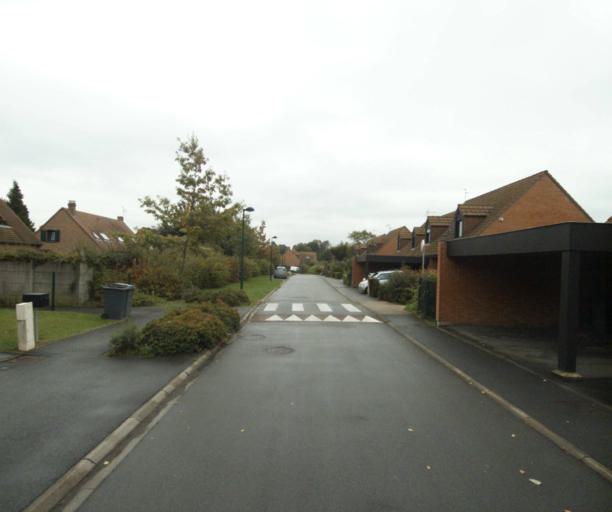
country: FR
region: Nord-Pas-de-Calais
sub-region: Departement du Nord
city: Santes
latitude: 50.5956
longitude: 2.9554
